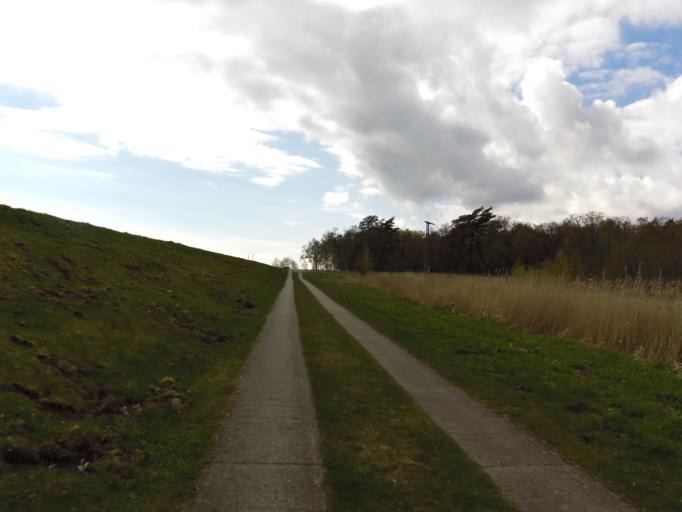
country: DE
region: Mecklenburg-Vorpommern
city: Barth
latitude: 54.4170
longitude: 12.7655
